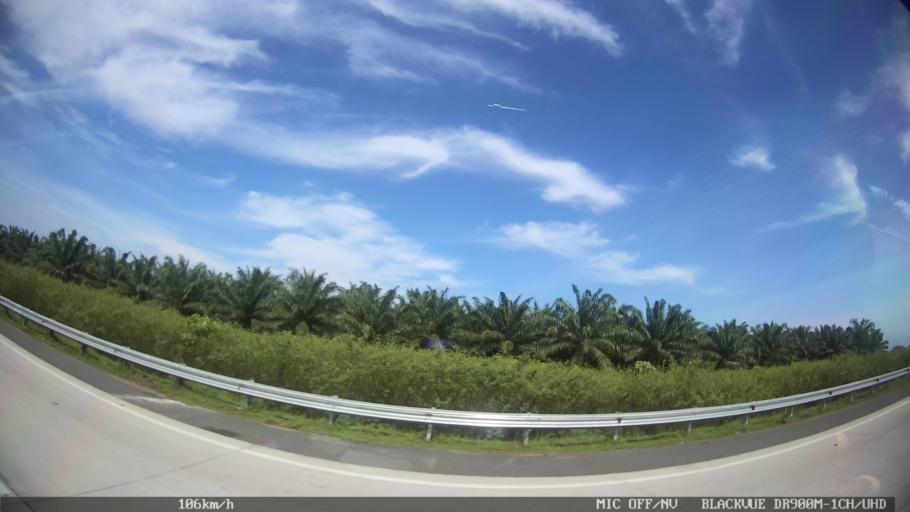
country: ID
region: North Sumatra
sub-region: Kabupaten Langkat
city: Stabat
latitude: 3.6890
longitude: 98.5394
